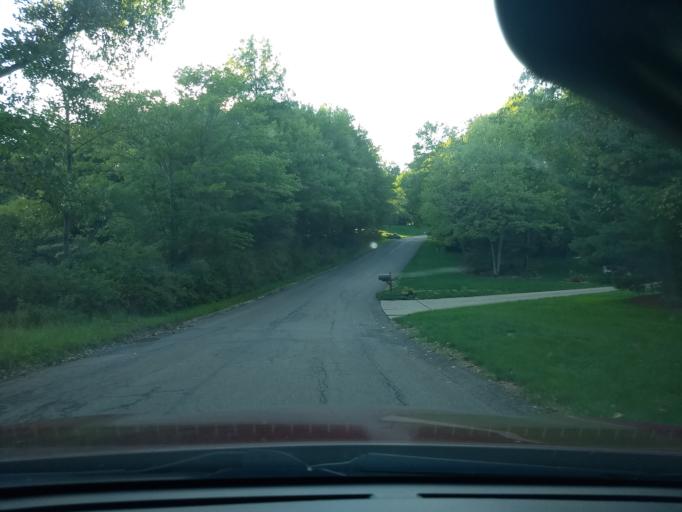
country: US
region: Pennsylvania
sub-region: Allegheny County
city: Gibsonia
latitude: 40.6396
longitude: -79.9612
